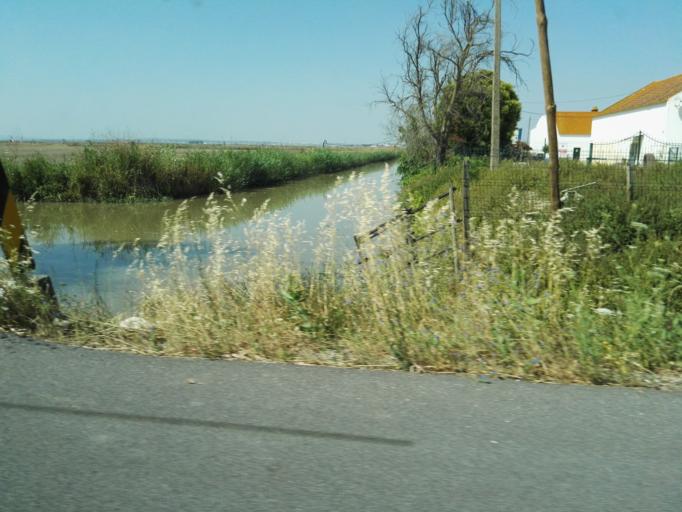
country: PT
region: Santarem
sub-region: Benavente
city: Samora Correia
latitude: 38.9349
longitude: -8.9228
